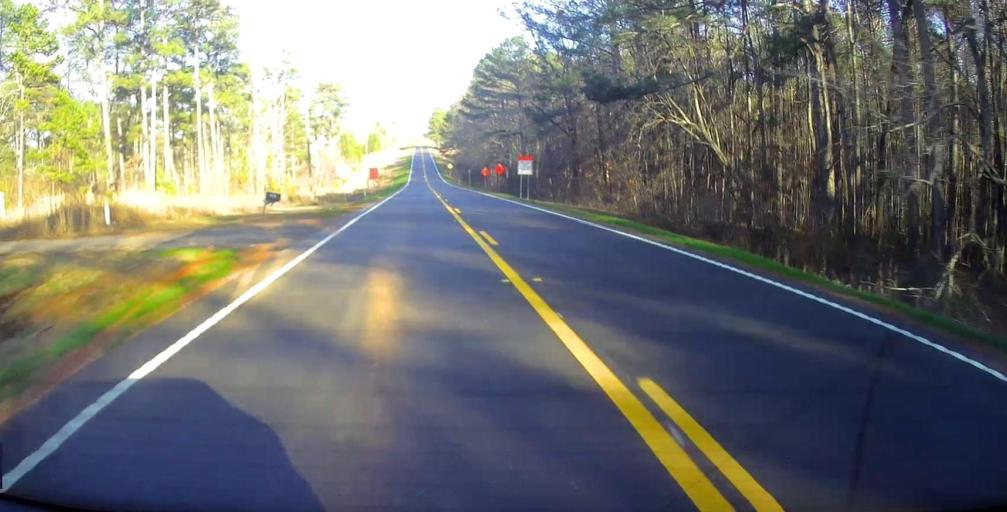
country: US
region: Georgia
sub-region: Harris County
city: Hamilton
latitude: 32.7472
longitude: -84.9884
